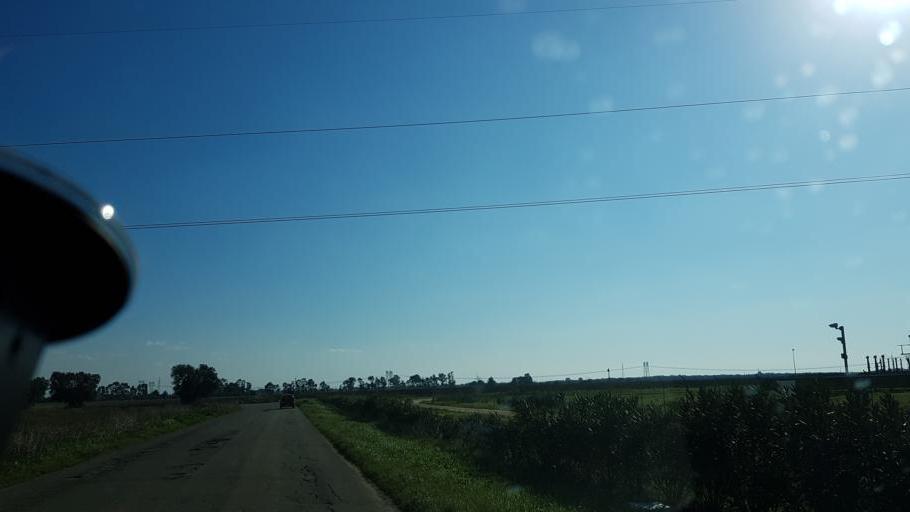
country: IT
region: Apulia
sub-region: Provincia di Brindisi
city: Brindisi
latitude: 40.6141
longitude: 17.8668
